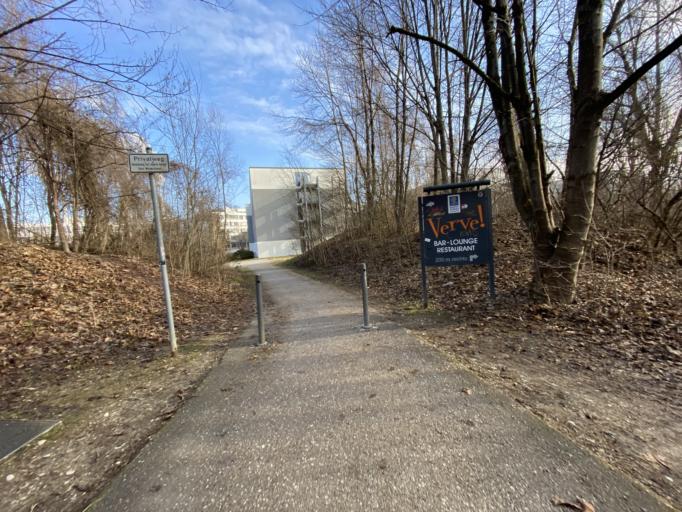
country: DE
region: Bavaria
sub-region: Upper Bavaria
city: Unterfoehring
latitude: 48.1739
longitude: 11.6390
